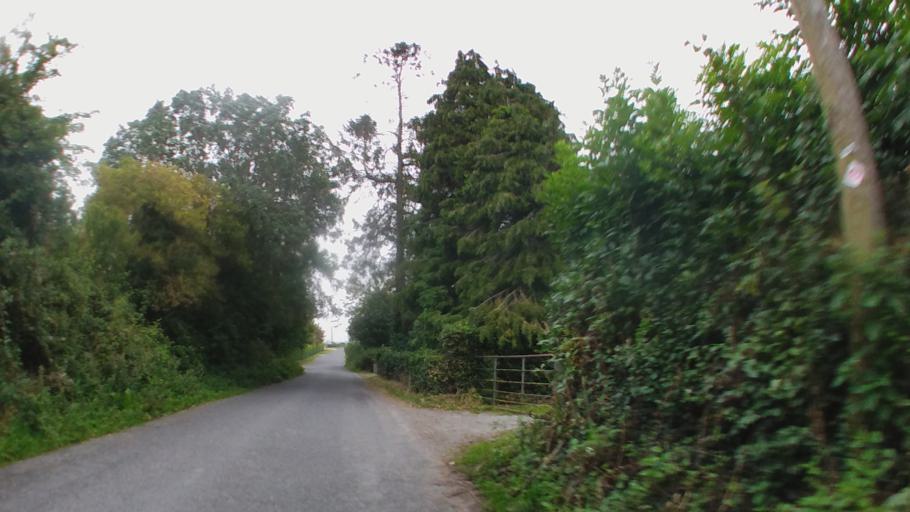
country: IE
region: Leinster
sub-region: Kilkenny
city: Kilkenny
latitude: 52.7018
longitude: -7.1913
